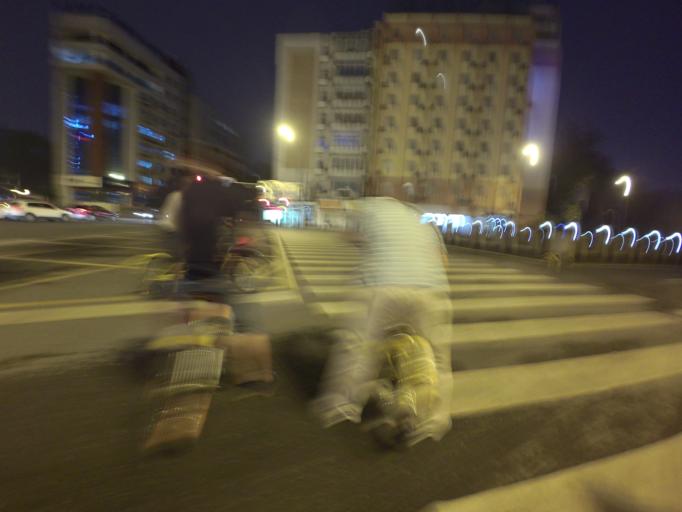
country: CN
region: Sichuan
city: Chengdu
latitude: 30.6693
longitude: 104.0582
